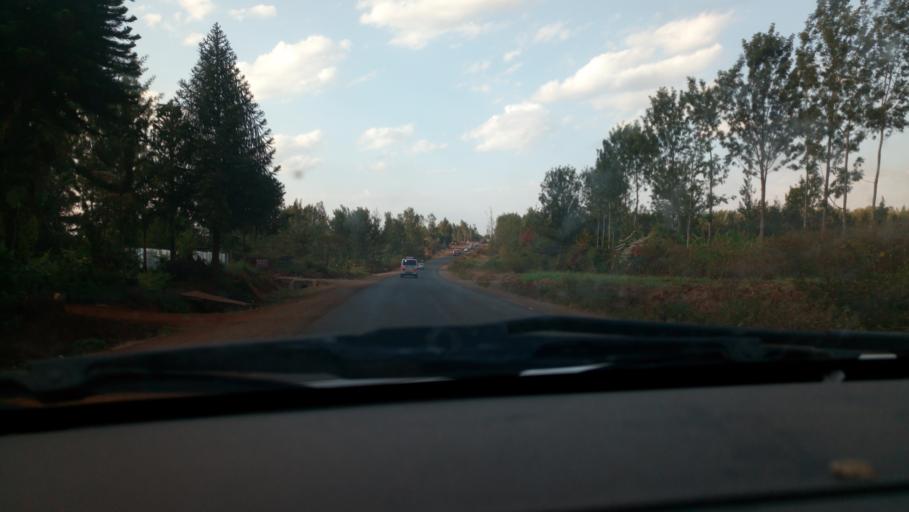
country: KE
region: Murang'a District
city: Maragua
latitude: -0.8324
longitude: 37.1374
